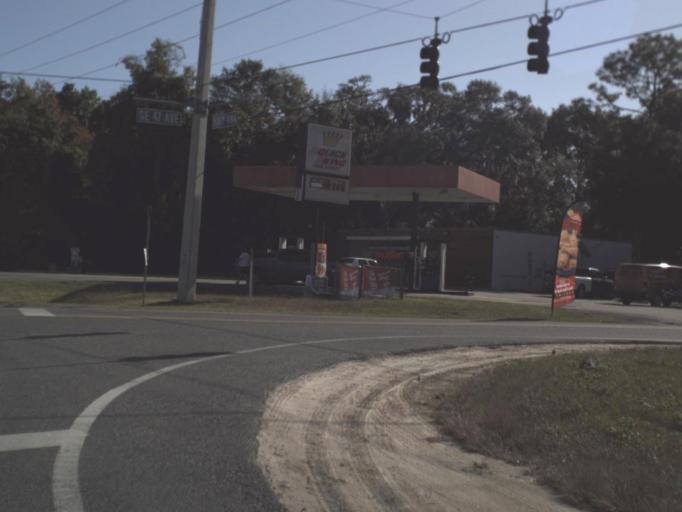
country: US
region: Florida
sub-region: Marion County
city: Belleview
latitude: 29.0263
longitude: -82.0706
